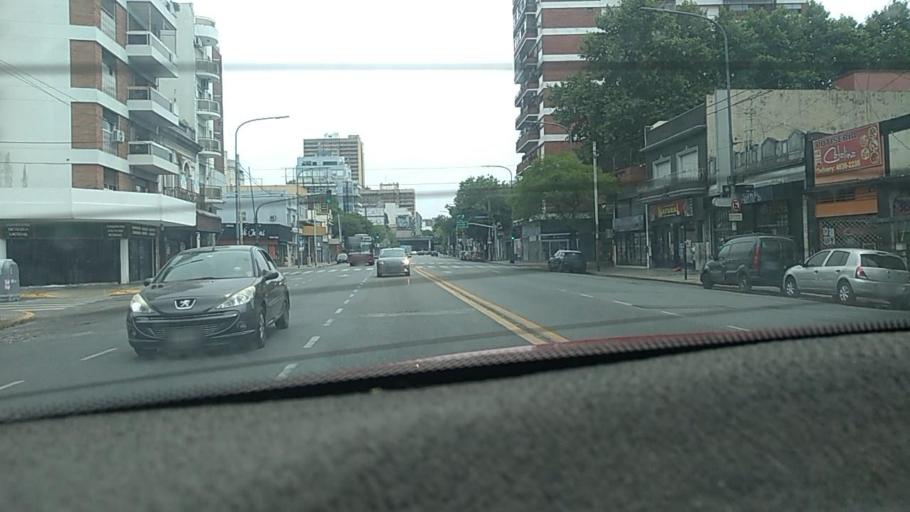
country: AR
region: Buenos Aires F.D.
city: Villa Santa Rita
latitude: -34.6361
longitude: -58.4915
